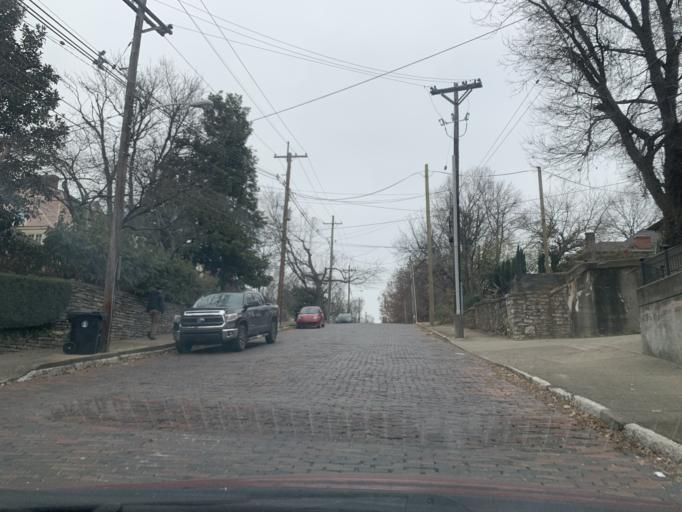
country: US
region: Kentucky
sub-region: Jefferson County
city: Indian Hills
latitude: 38.2496
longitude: -85.6972
